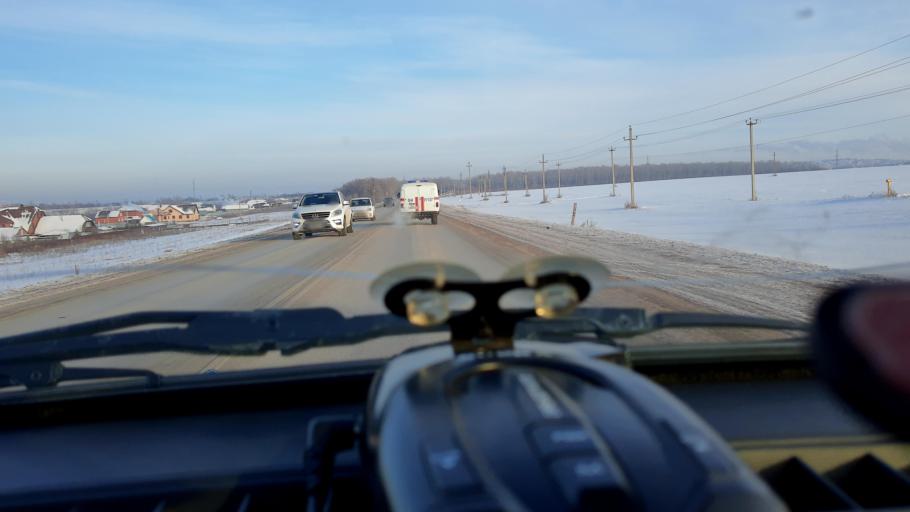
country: RU
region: Bashkortostan
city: Avdon
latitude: 54.6069
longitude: 55.8609
